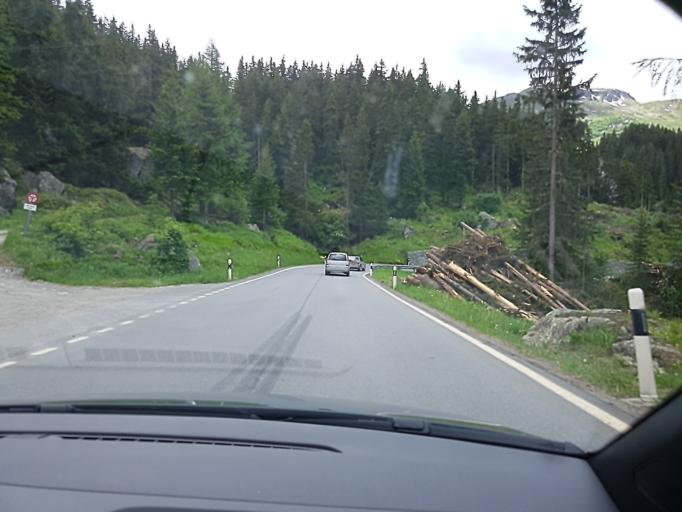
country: CH
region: Grisons
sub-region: Maloja District
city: Silvaplana
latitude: 46.4904
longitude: 9.6427
